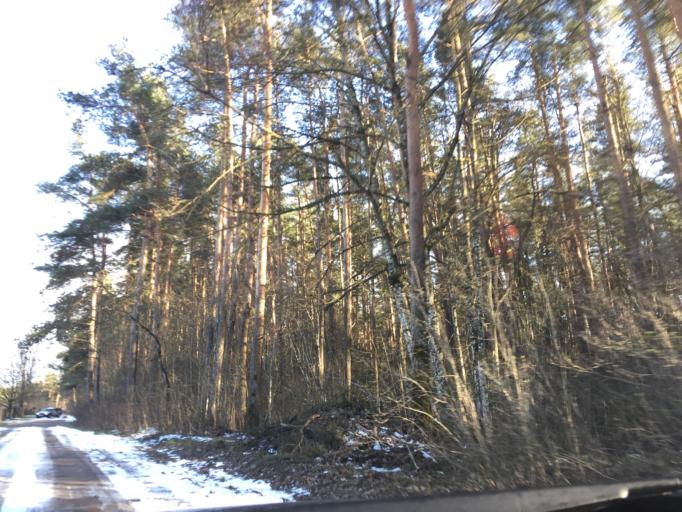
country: LV
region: Kekava
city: Kekava
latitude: 56.8458
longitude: 24.1917
